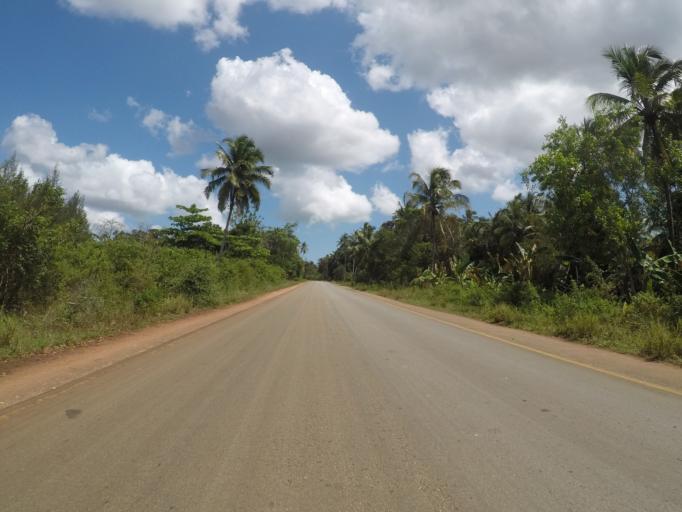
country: TZ
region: Zanzibar Central/South
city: Koani
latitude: -6.1706
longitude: 39.3300
